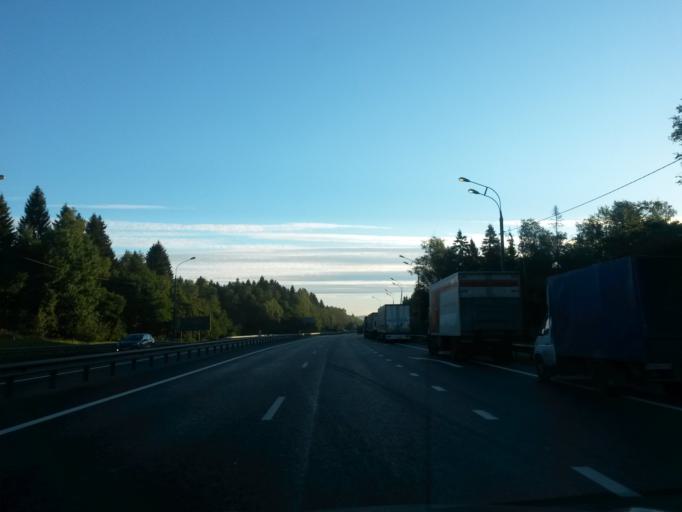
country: RU
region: Moskovskaya
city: Svatkovo
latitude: 56.3446
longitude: 38.2671
